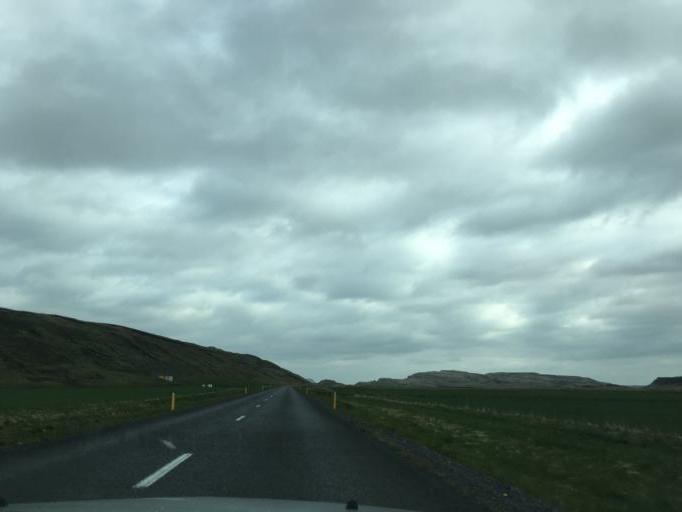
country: IS
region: South
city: Vestmannaeyjar
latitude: 64.2209
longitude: -20.2590
